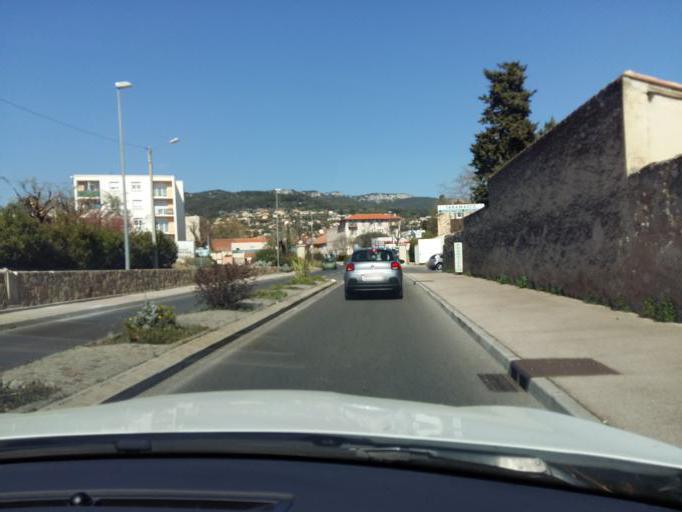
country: FR
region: Provence-Alpes-Cote d'Azur
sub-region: Departement du Var
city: Ollioules
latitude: 43.1317
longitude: 5.8447
